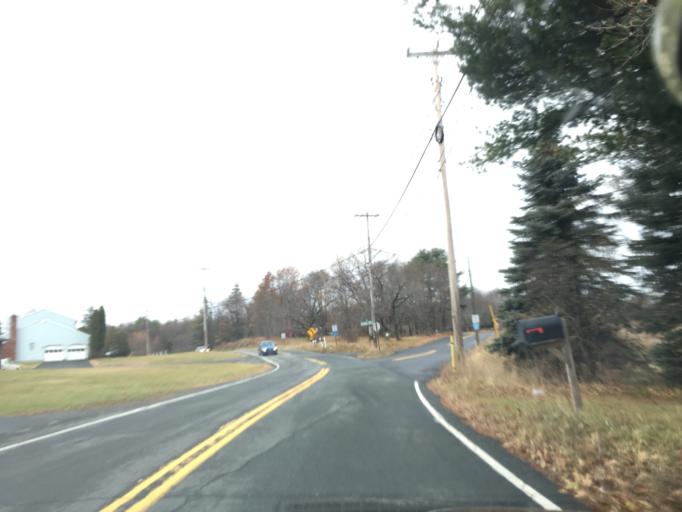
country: US
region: New York
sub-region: Rensselaer County
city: Wynantskill
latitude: 42.6675
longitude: -73.6428
